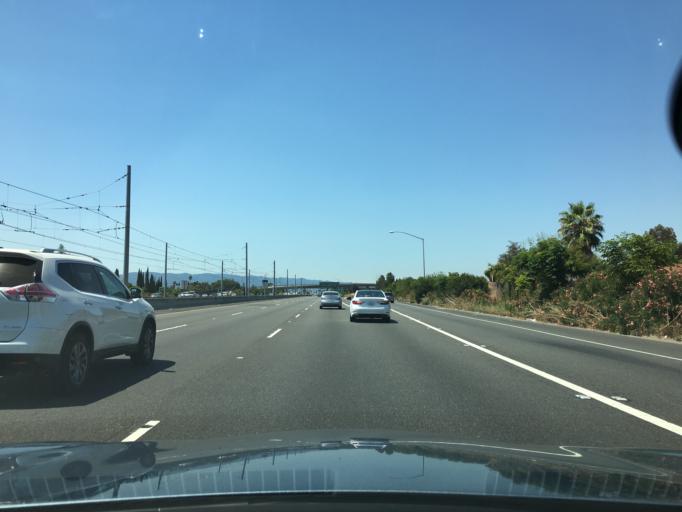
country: US
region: California
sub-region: Santa Clara County
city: Seven Trees
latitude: 37.2555
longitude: -121.8496
